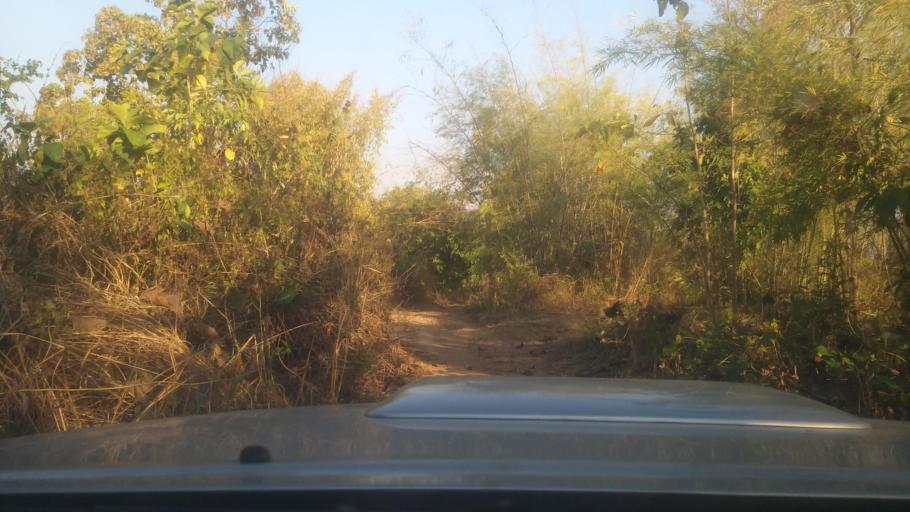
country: TH
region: Phrae
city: Nong Muang Khai
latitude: 18.2856
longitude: 100.0274
